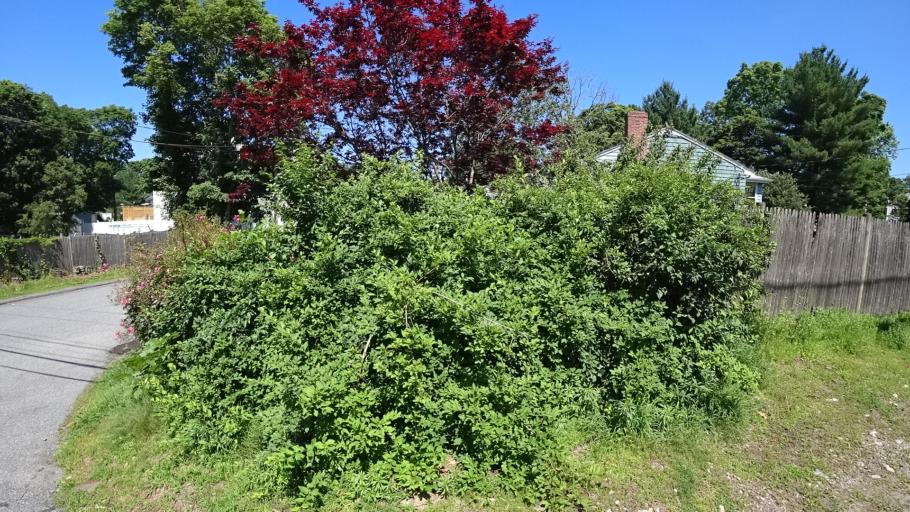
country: US
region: Massachusetts
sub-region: Norfolk County
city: Dedham
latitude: 42.2507
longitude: -71.1520
